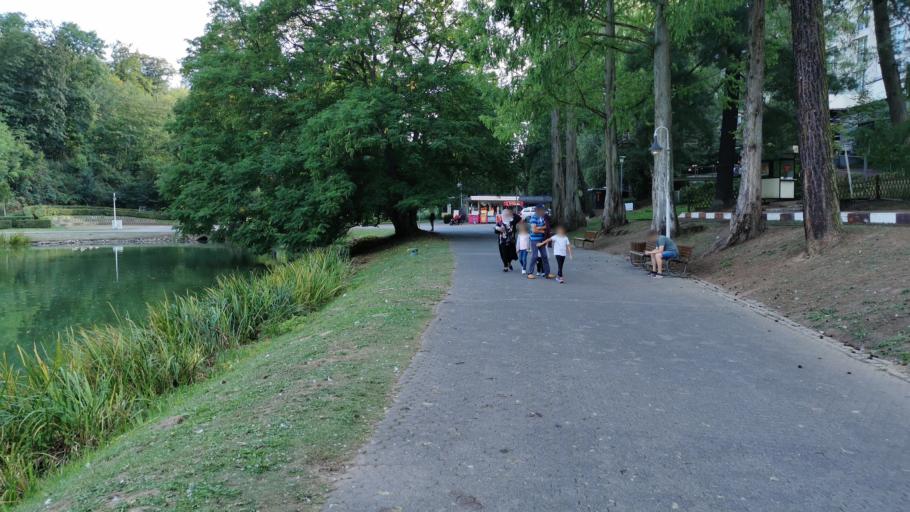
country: DE
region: Saarland
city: Saarbrucken
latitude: 49.2262
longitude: 6.9622
